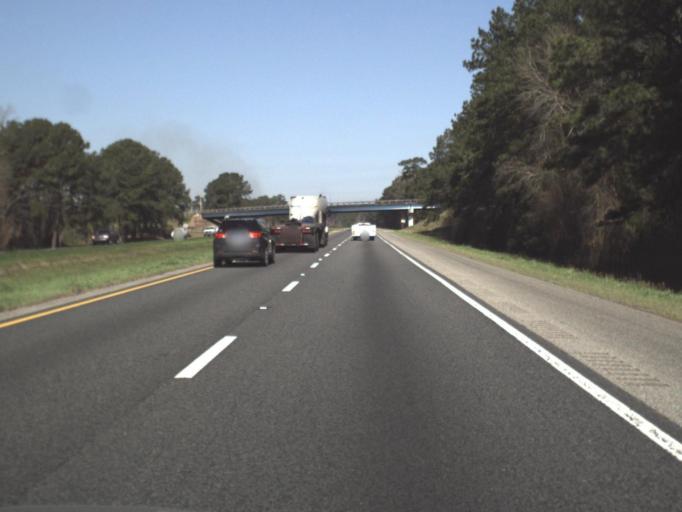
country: US
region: Florida
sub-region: Gadsden County
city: Gretna
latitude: 30.5938
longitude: -84.7224
